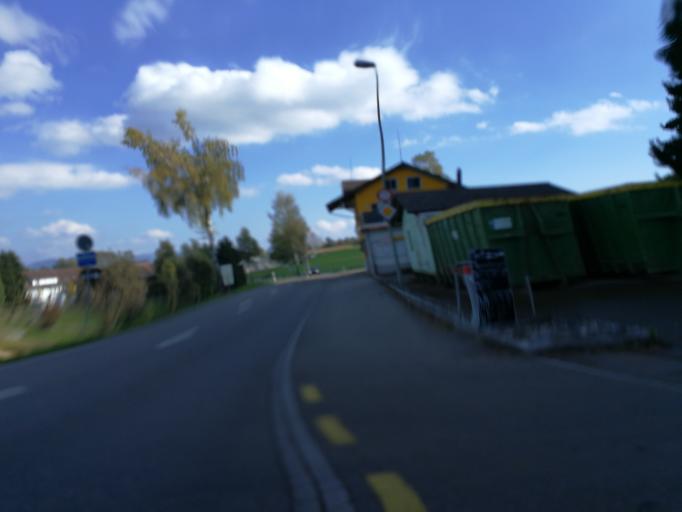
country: CH
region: Zurich
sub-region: Bezirk Meilen
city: Oetwil am See
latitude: 47.2656
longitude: 8.7318
